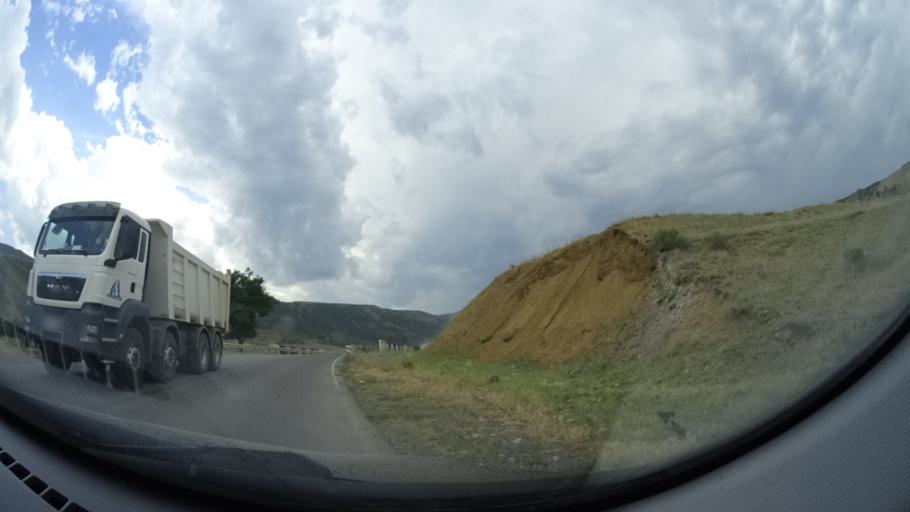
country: GE
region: Samtskhe-Javakheti
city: Aspindza
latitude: 41.5963
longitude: 43.1911
